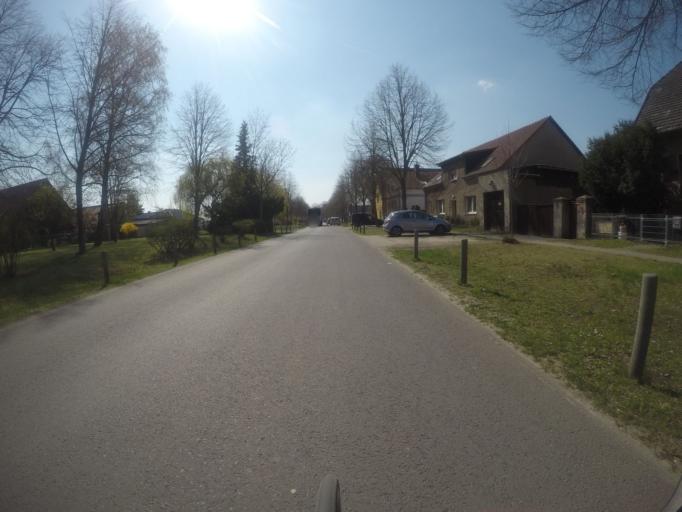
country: DE
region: Brandenburg
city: Falkensee
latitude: 52.6187
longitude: 13.1266
